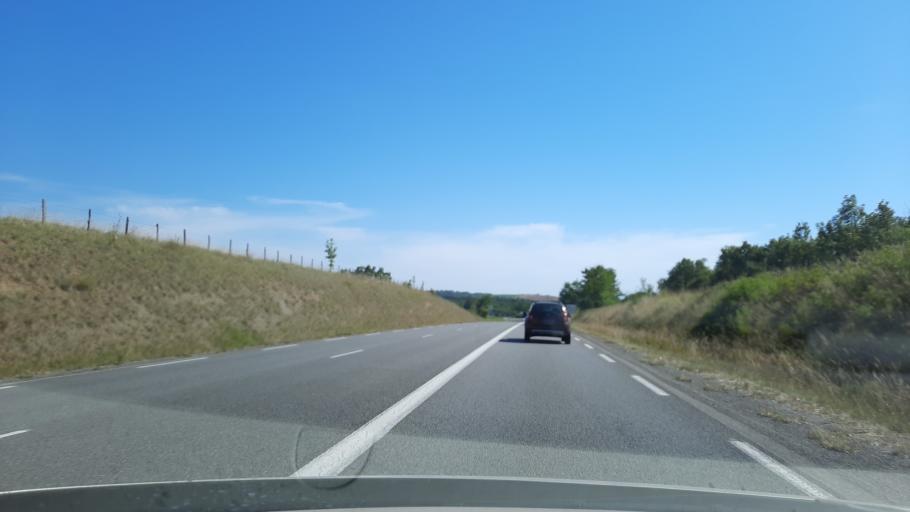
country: FR
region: Midi-Pyrenees
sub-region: Departement de l'Aveyron
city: Villefranche-de-Rouergue
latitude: 44.3336
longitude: 1.9341
